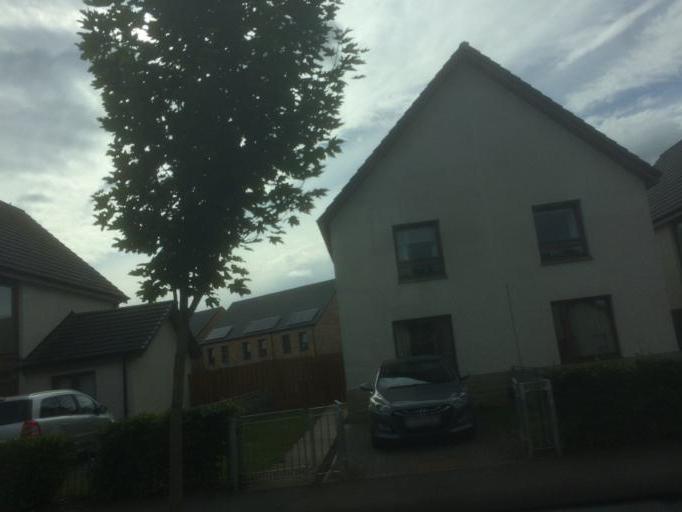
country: GB
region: Scotland
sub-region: Perth and Kinross
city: Perth
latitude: 56.4083
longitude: -3.4414
